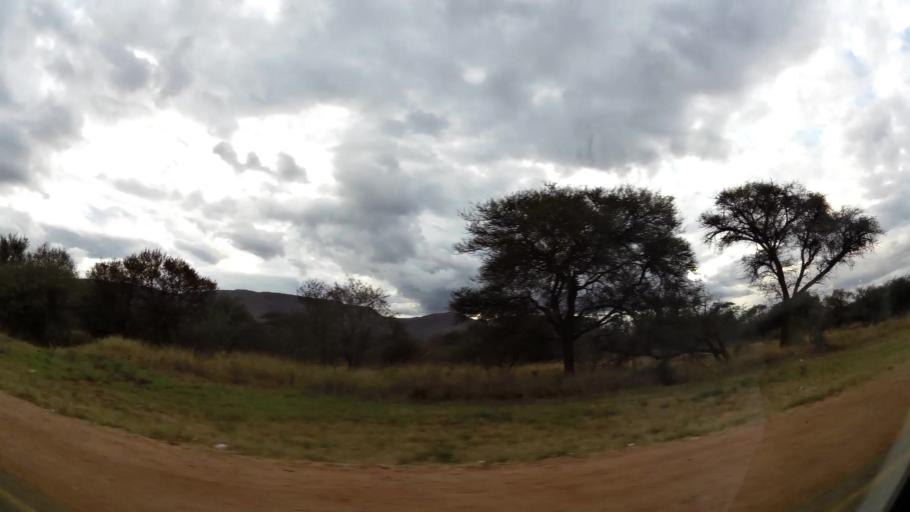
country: ZA
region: Limpopo
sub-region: Waterberg District Municipality
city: Mokopane
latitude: -24.2321
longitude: 28.9986
